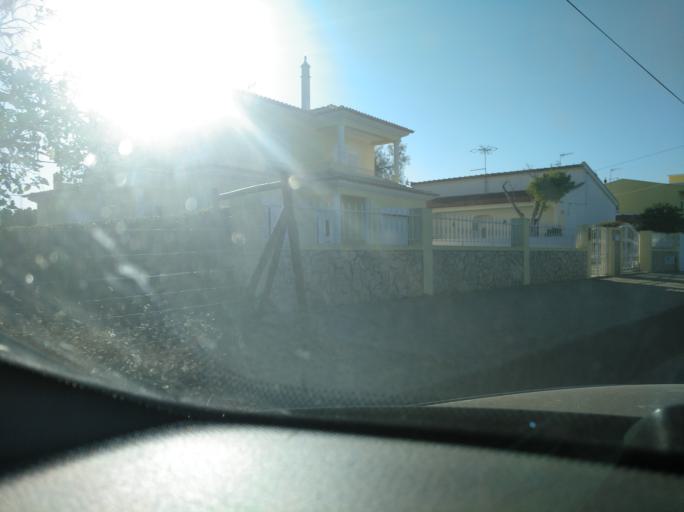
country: PT
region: Faro
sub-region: Vila Real de Santo Antonio
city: Monte Gordo
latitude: 37.1834
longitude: -7.5224
